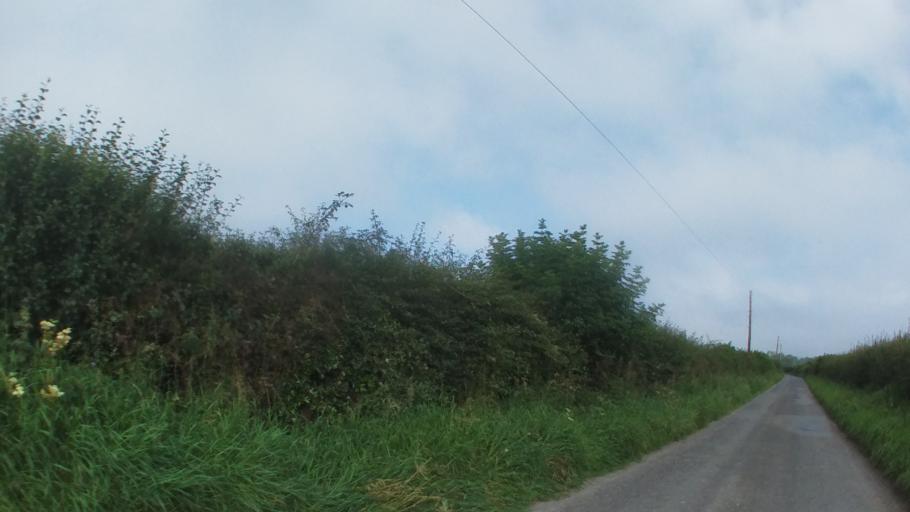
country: IE
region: Leinster
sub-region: Kilkenny
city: Kilkenny
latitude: 52.6937
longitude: -7.1902
